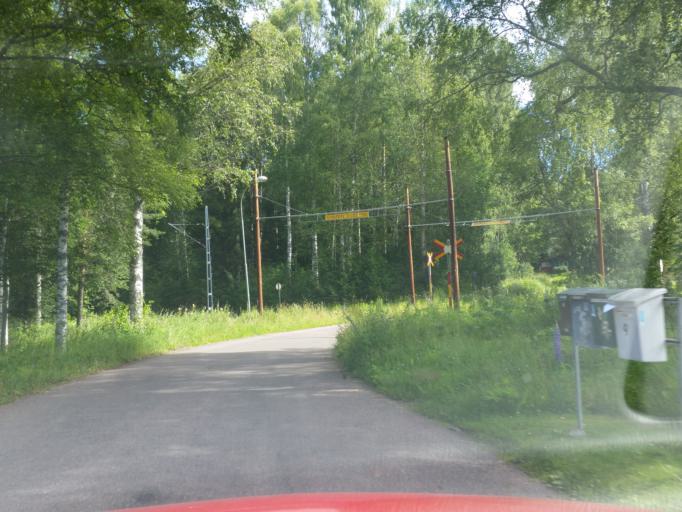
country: SE
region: Dalarna
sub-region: Leksand Municipality
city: Smedby
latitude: 60.6669
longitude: 15.1037
